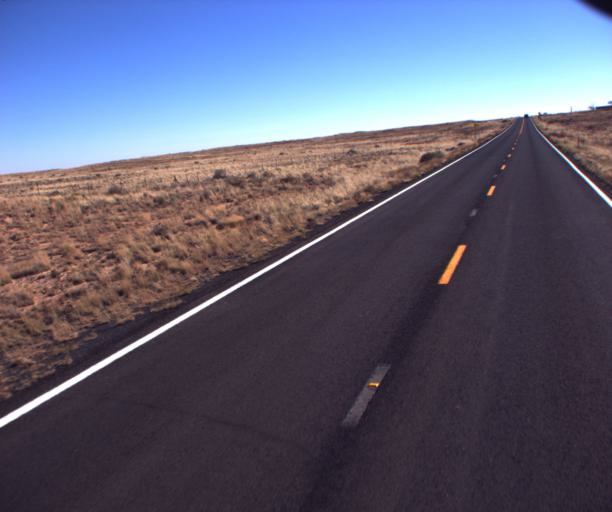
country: US
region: Arizona
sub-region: Coconino County
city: Tuba City
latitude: 35.9625
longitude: -110.9432
